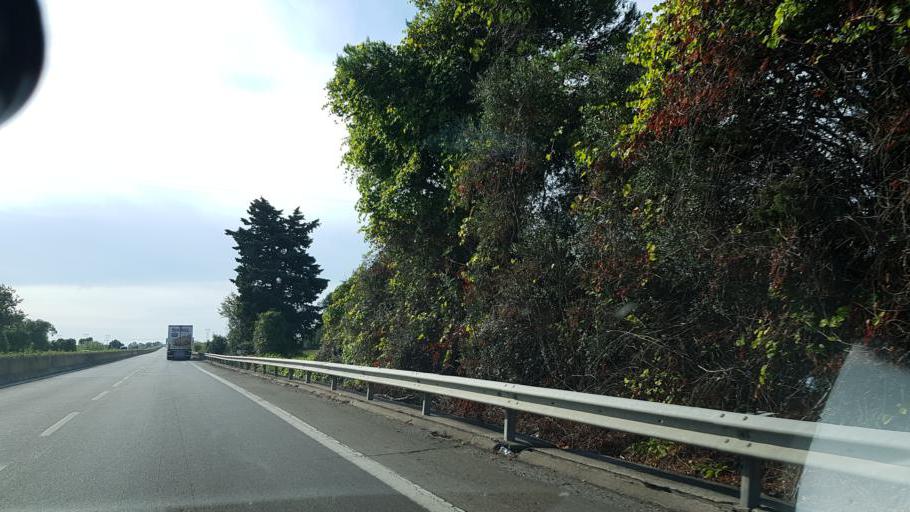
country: IT
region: Apulia
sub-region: Provincia di Brindisi
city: La Rosa
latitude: 40.5756
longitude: 17.9811
